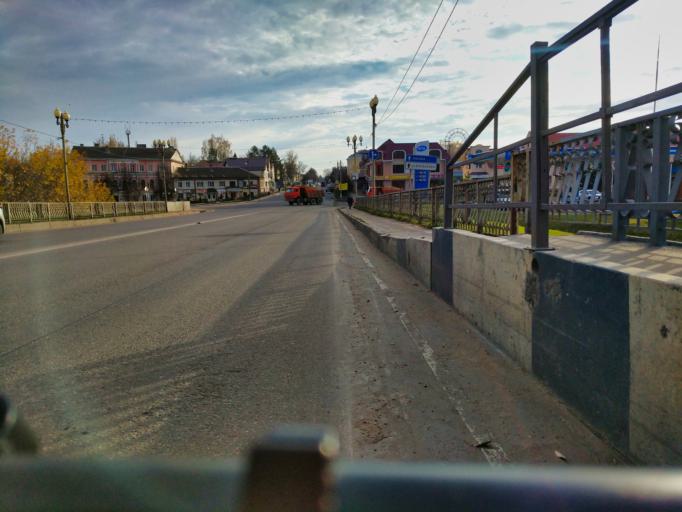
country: RU
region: Tverskaya
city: Rzhev
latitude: 56.2594
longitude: 34.3284
